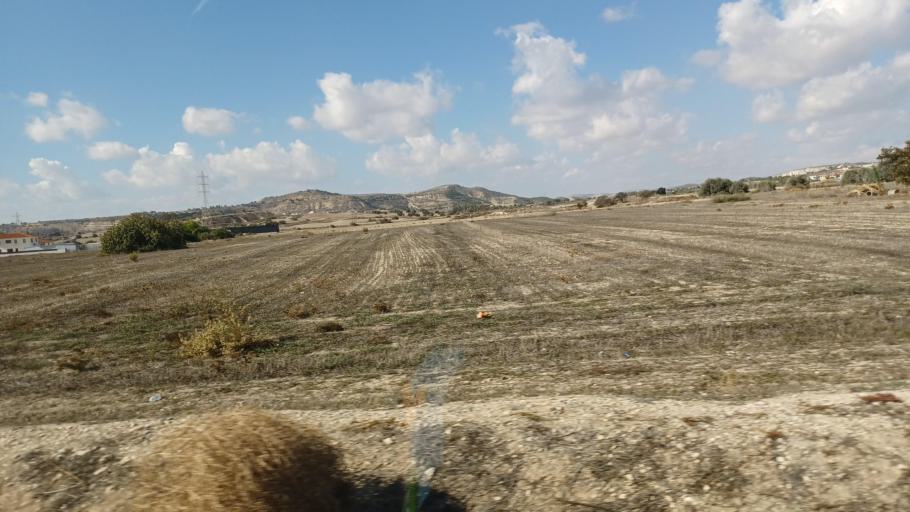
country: CY
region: Larnaka
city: Voroklini
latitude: 34.9880
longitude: 33.6804
